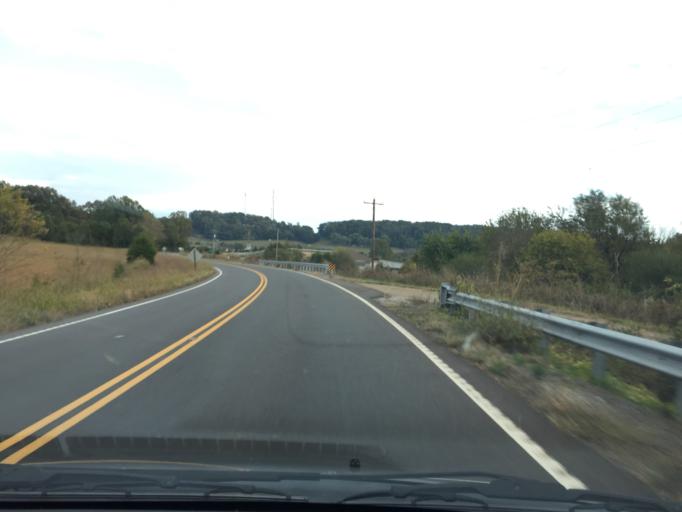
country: US
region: Tennessee
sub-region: Monroe County
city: Sweetwater
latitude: 35.6250
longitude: -84.4985
